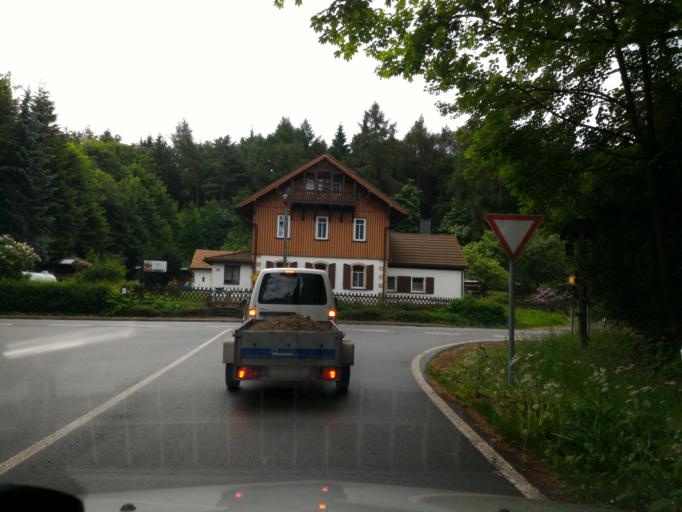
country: DE
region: Saxony
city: Kurort Oybin
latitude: 50.8290
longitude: 14.7844
